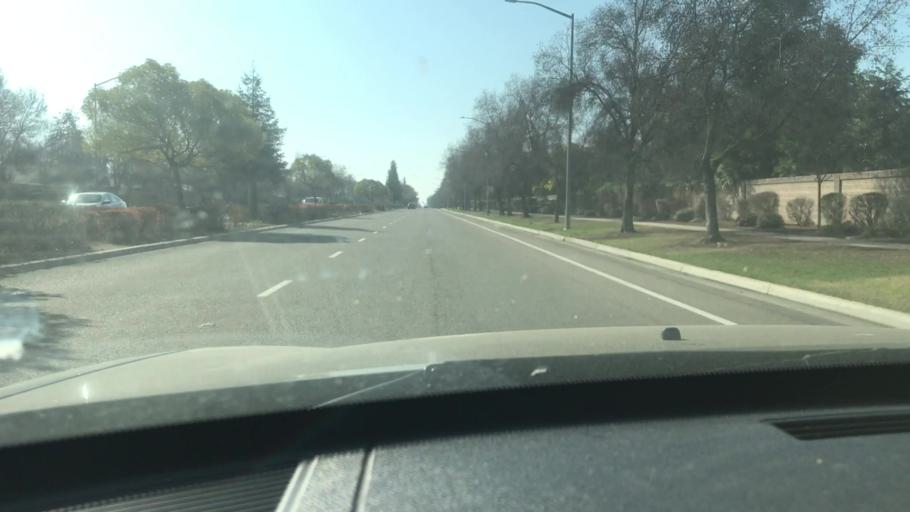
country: US
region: California
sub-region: Fresno County
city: Tarpey Village
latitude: 36.8072
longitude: -119.6640
